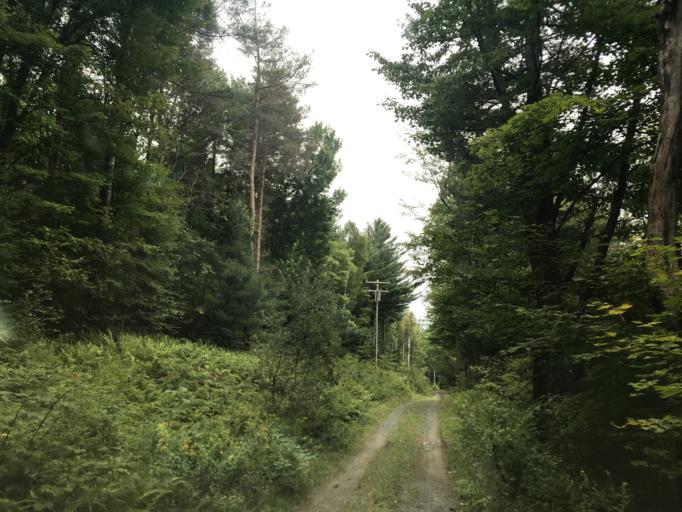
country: US
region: New York
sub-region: Otsego County
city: Worcester
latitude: 42.5324
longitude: -74.6603
